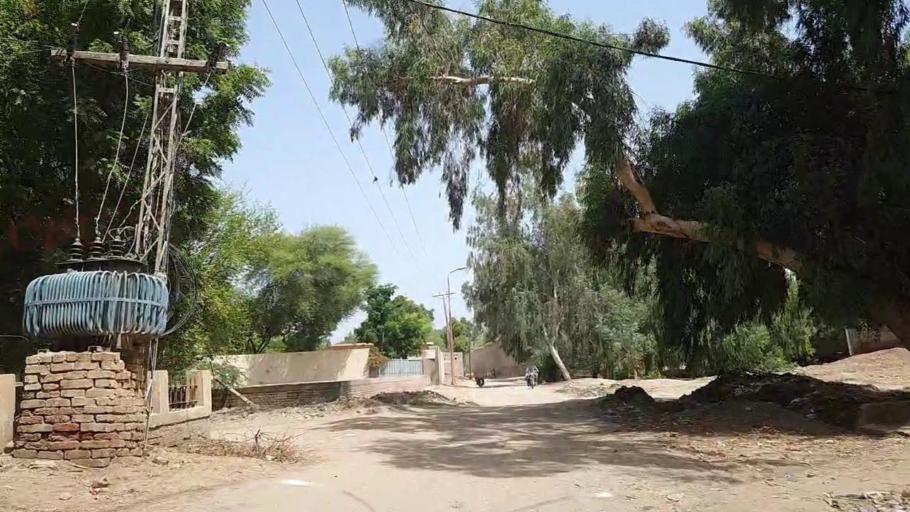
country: PK
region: Sindh
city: Tharu Shah
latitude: 27.0148
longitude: 68.1243
